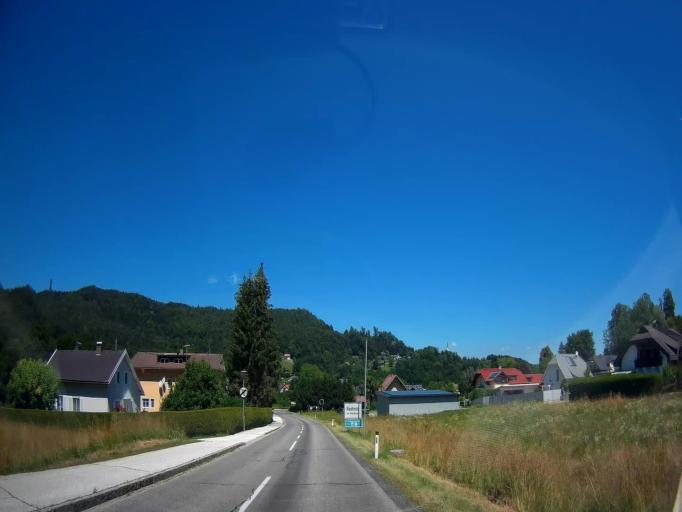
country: AT
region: Carinthia
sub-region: Politischer Bezirk Klagenfurt Land
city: Keutschach am See
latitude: 46.5992
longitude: 14.1745
